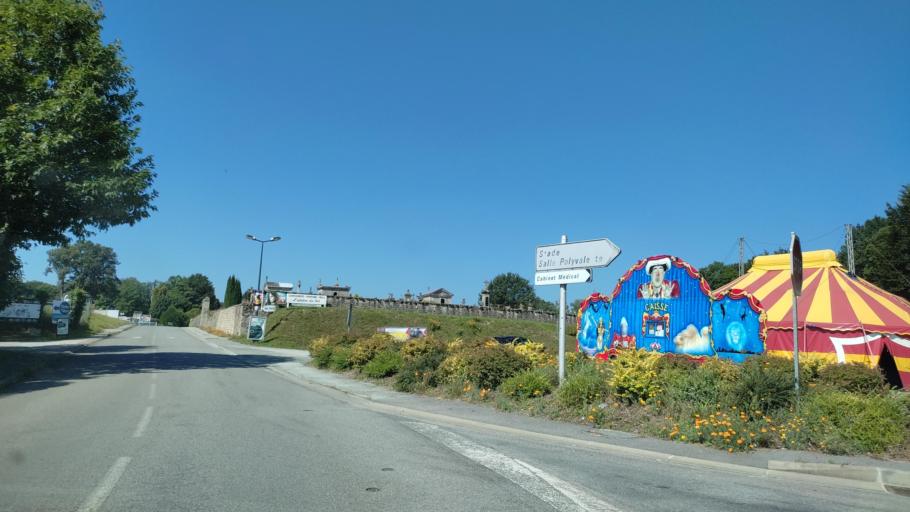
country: FR
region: Limousin
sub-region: Departement de la Haute-Vienne
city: Razes
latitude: 46.0326
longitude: 1.3417
